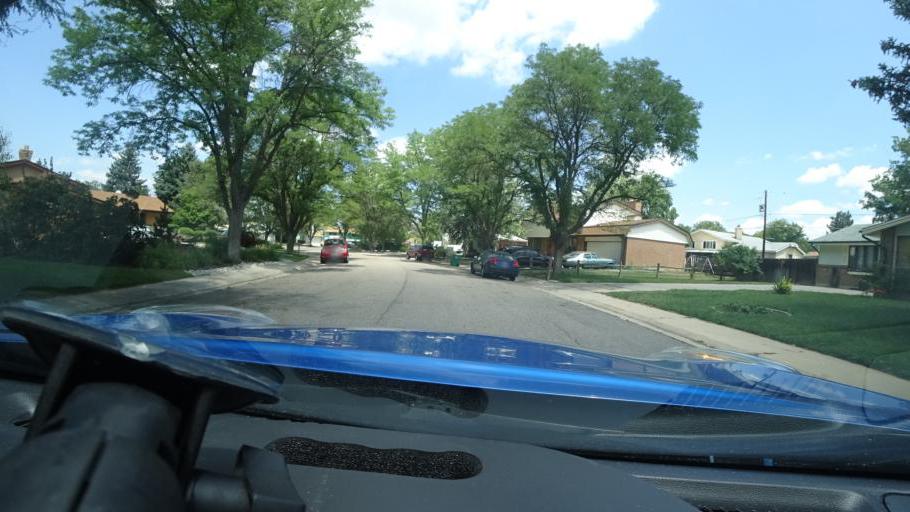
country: US
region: Colorado
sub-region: Adams County
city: Aurora
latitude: 39.7026
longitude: -104.8398
